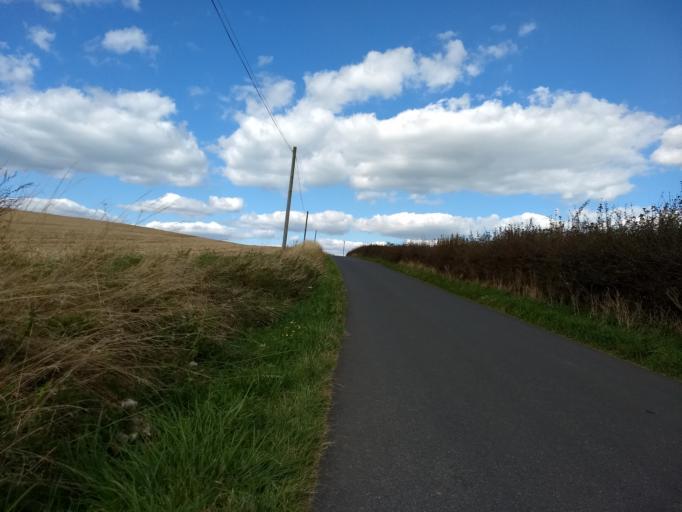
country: GB
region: England
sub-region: Isle of Wight
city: Shalfleet
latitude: 50.6719
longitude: -1.4388
